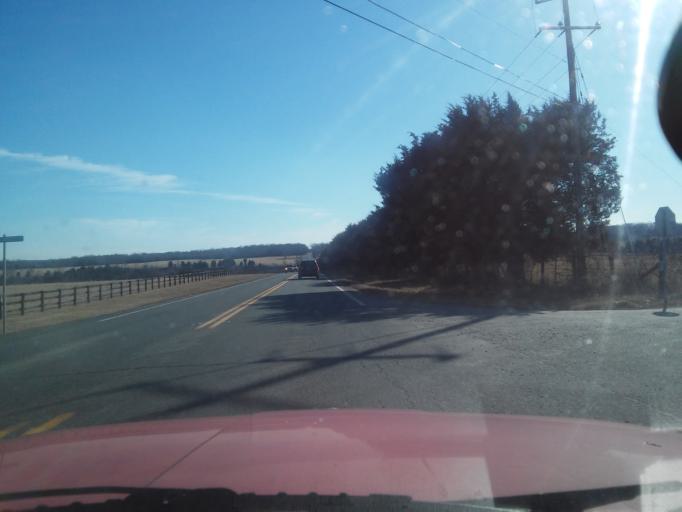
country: US
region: Virginia
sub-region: Orange County
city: Gordonsville
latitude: 38.0250
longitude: -78.1905
